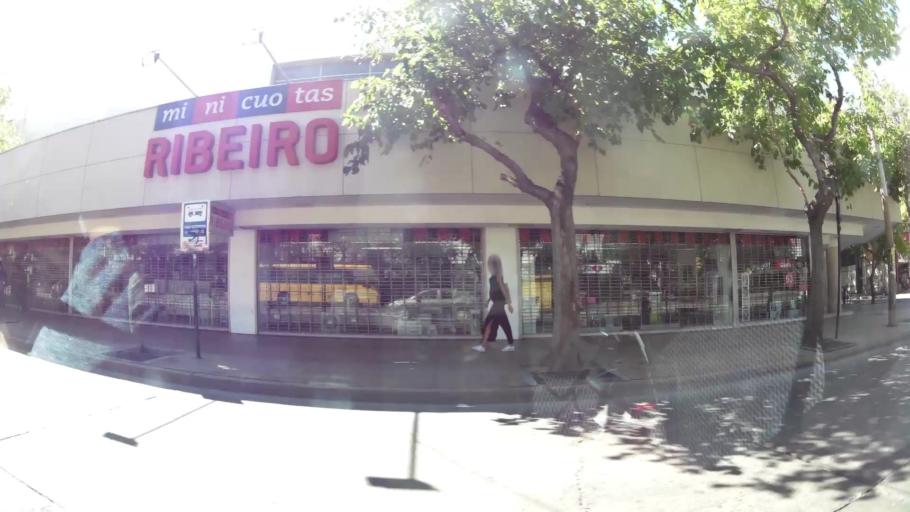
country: AR
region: San Juan
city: San Juan
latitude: -31.5340
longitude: -68.5236
